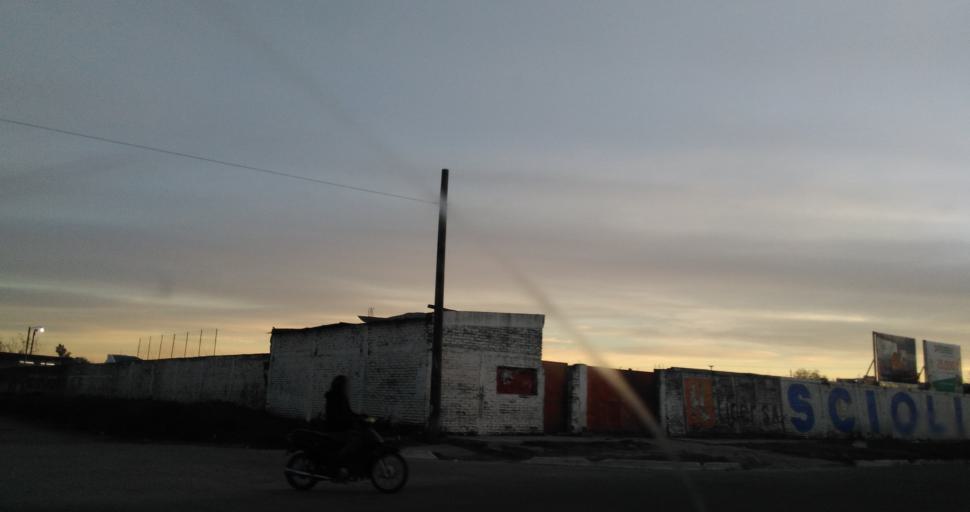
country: AR
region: Chaco
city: Resistencia
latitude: -27.4662
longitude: -59.0033
